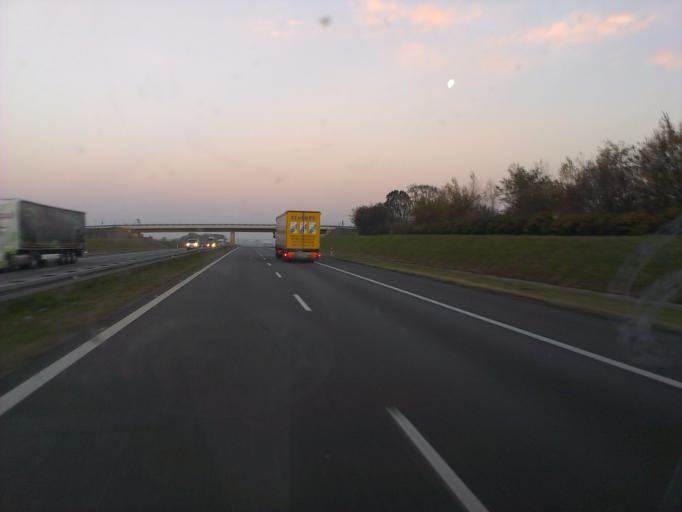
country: PL
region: Opole Voivodeship
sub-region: Powiat strzelecki
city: Strzelce Opolskie
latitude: 50.4587
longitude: 18.2527
